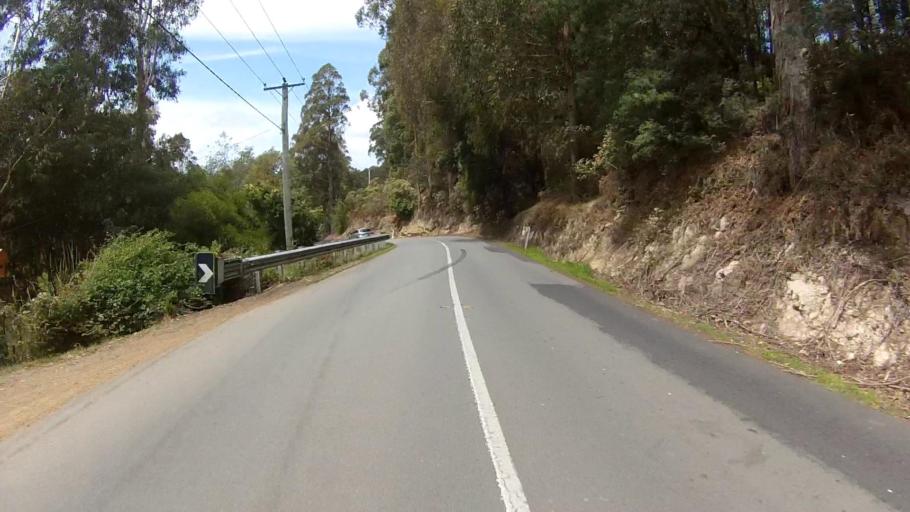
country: AU
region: Tasmania
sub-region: Kingborough
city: Kettering
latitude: -43.1033
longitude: 147.2144
